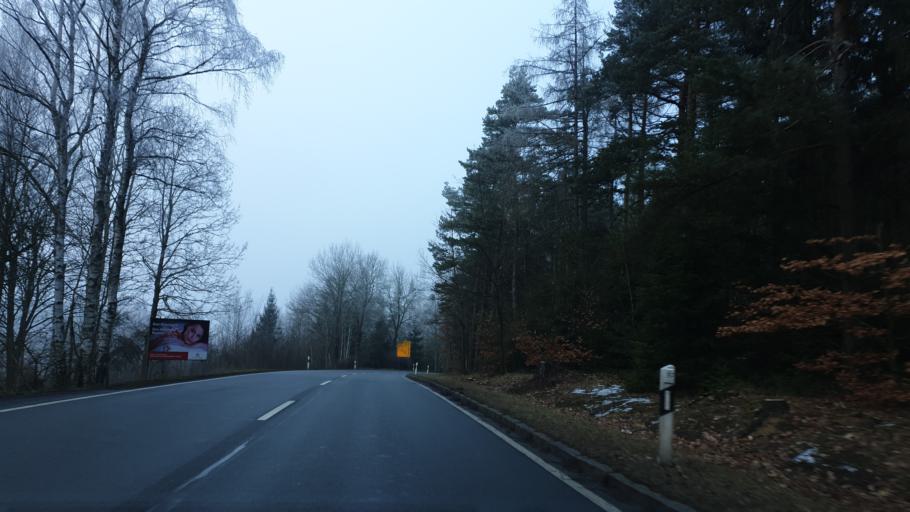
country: DE
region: Saxony
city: Bad Brambach
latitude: 50.2087
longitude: 12.3110
